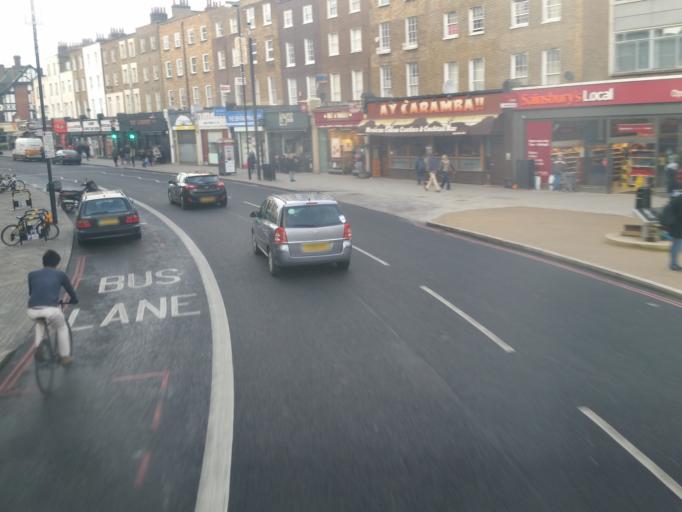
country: GB
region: England
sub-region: Greater London
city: Camden Town
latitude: 51.5348
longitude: -0.1390
